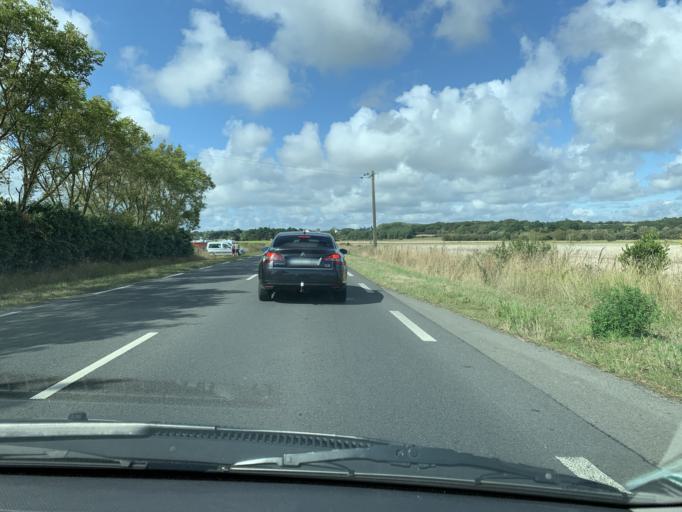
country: FR
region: Pays de la Loire
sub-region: Departement de la Loire-Atlantique
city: Guerande
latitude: 47.3072
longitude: -2.4302
